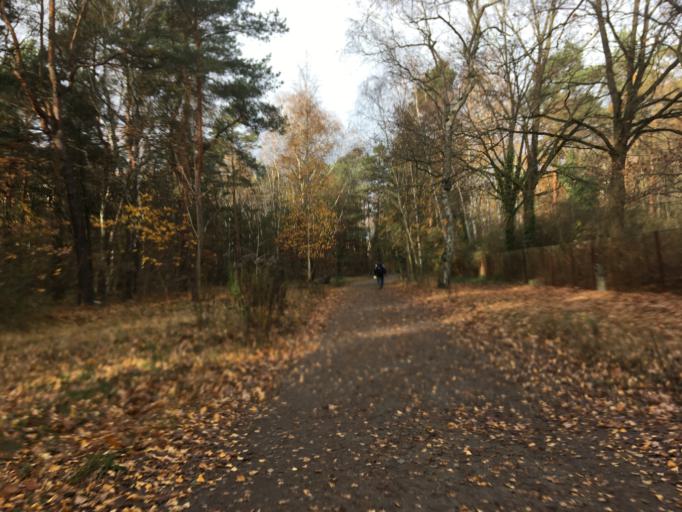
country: DE
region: Berlin
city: Adlershof
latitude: 52.4463
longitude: 13.5402
